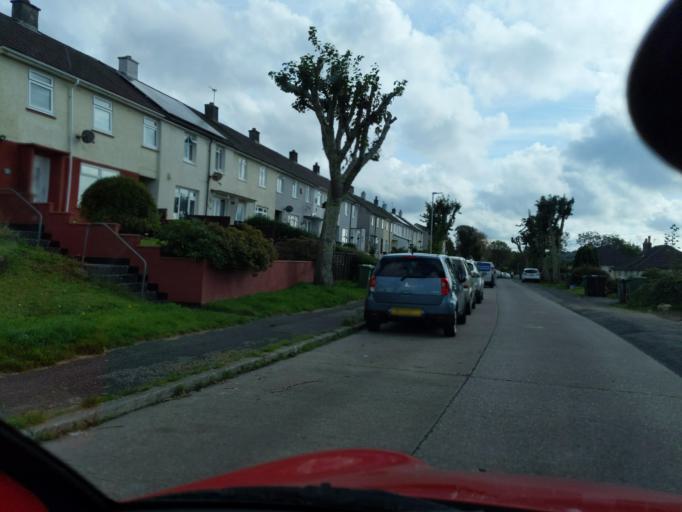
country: GB
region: England
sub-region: Plymouth
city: Plymouth
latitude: 50.4215
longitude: -4.1634
